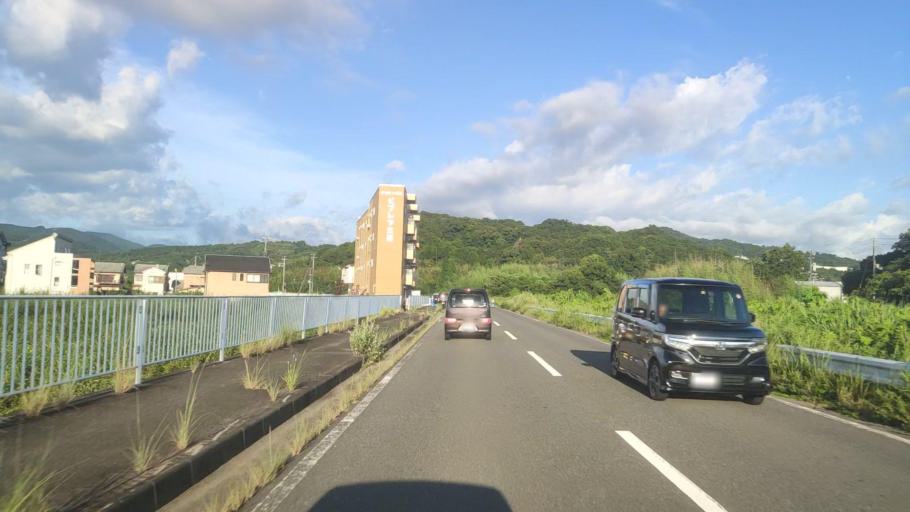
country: JP
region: Wakayama
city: Tanabe
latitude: 33.7331
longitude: 135.4168
